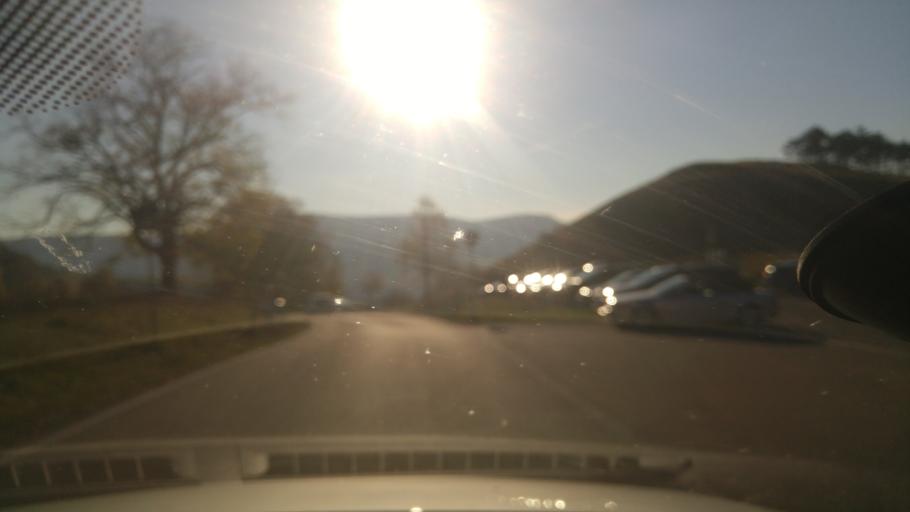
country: DE
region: Baden-Wuerttemberg
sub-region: Regierungsbezirk Stuttgart
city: Owen
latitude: 48.5943
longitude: 9.4682
